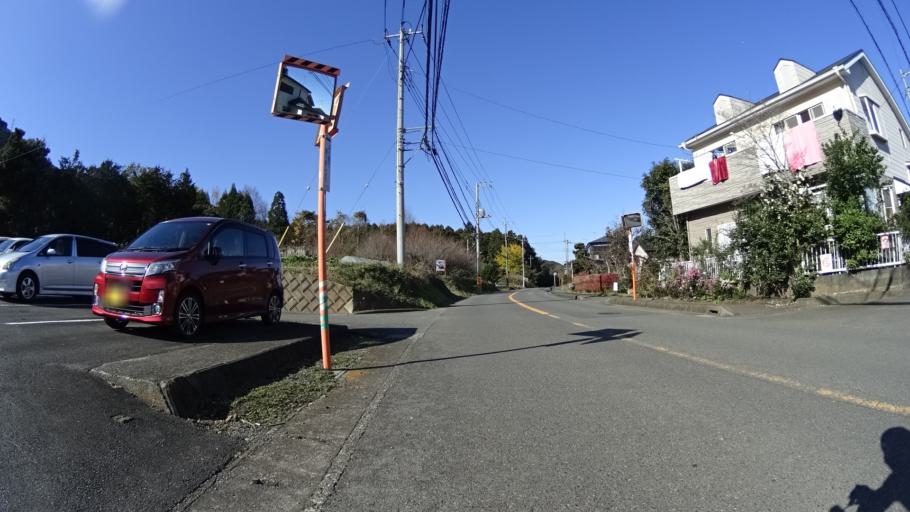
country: JP
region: Kanagawa
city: Zama
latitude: 35.5305
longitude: 139.2706
